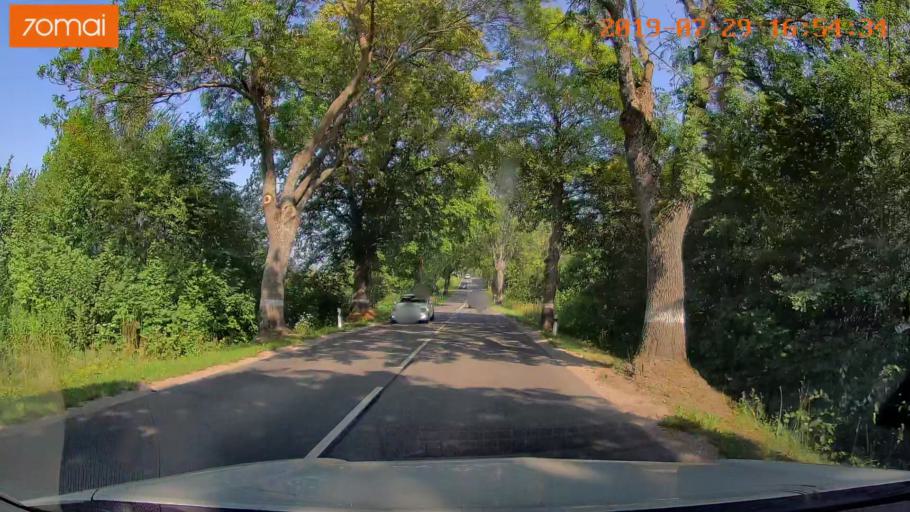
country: RU
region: Kaliningrad
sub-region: Gorod Svetlogorsk
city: Svetlogorsk
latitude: 54.8129
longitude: 20.1335
